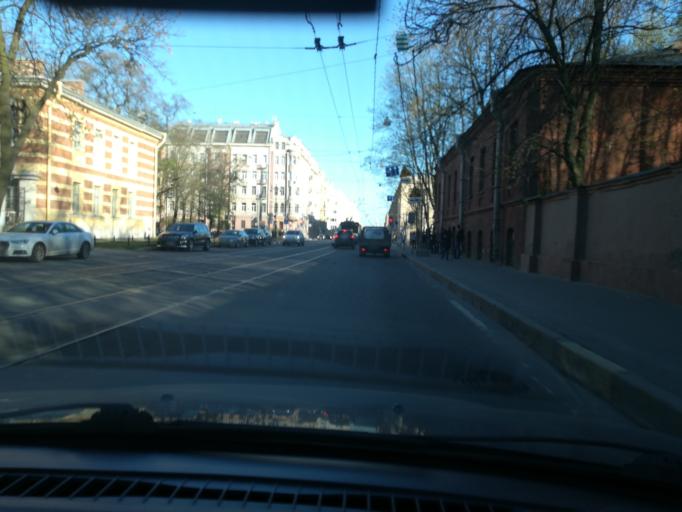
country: RU
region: St.-Petersburg
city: Vasyl'evsky Ostrov
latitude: 59.9338
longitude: 30.2615
